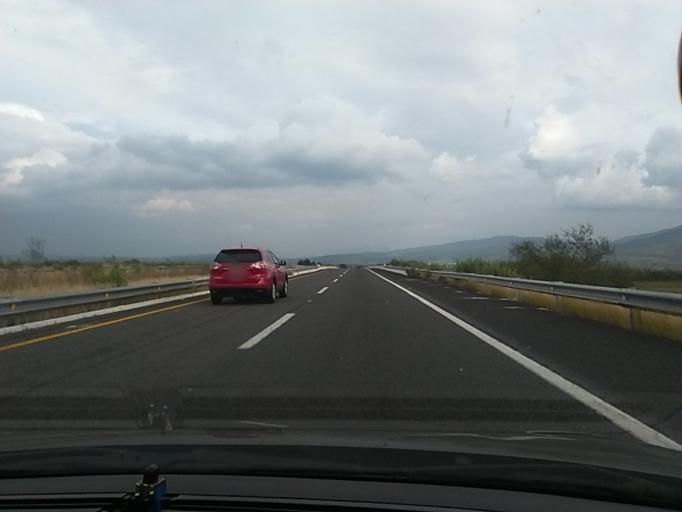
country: MX
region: Michoacan
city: Ecuandureo
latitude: 20.1790
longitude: -102.2662
